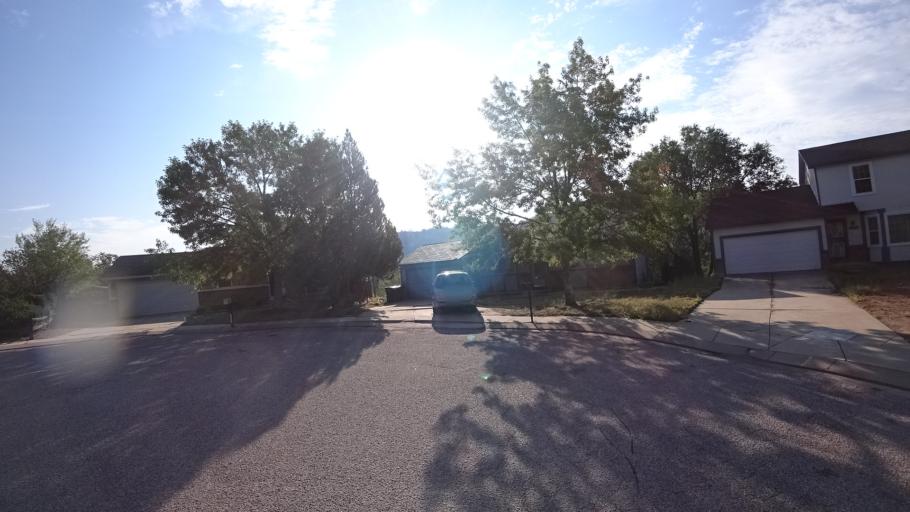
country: US
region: Colorado
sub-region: El Paso County
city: Colorado Springs
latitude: 38.8860
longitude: -104.7888
